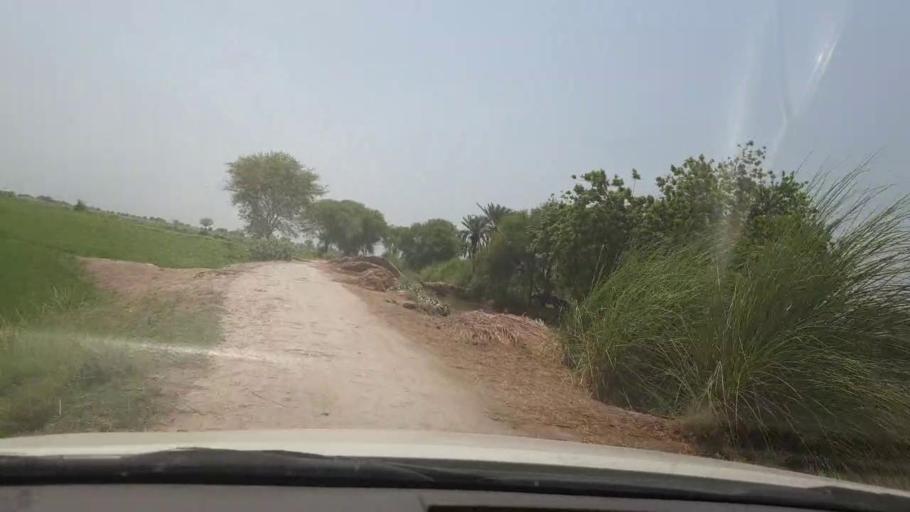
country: PK
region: Sindh
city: Shikarpur
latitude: 28.0783
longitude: 68.5497
